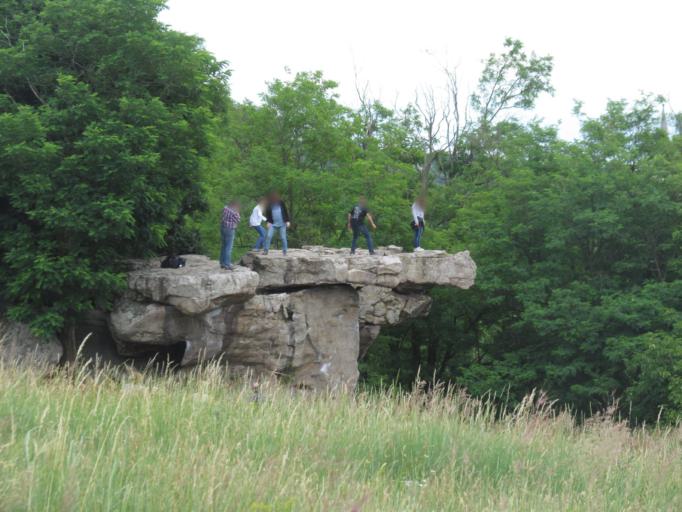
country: HU
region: Veszprem
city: Revfueloep
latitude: 46.8896
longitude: 17.5549
